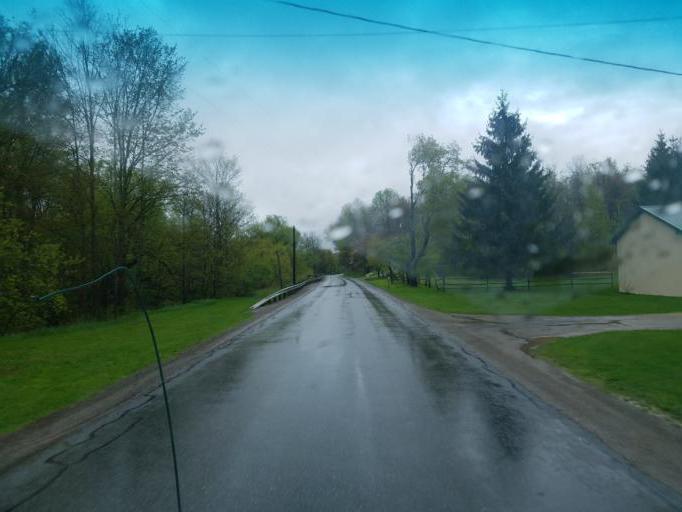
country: US
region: Pennsylvania
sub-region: Tioga County
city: Westfield
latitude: 41.9531
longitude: -77.6475
